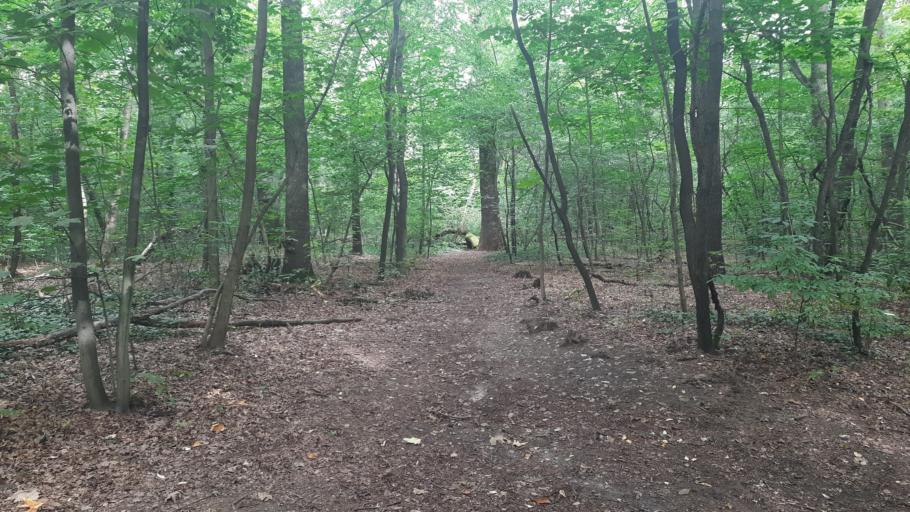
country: PL
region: Lodz Voivodeship
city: Lodz
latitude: 51.8078
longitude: 19.4473
